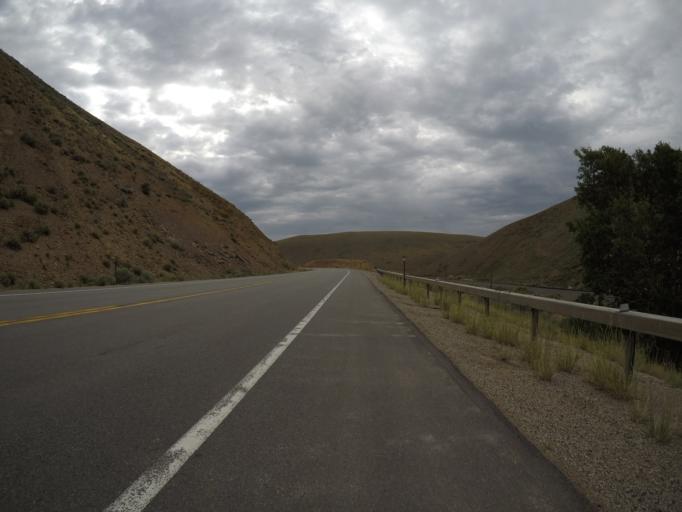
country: US
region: Wyoming
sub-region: Lincoln County
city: Kemmerer
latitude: 41.8238
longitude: -110.8230
